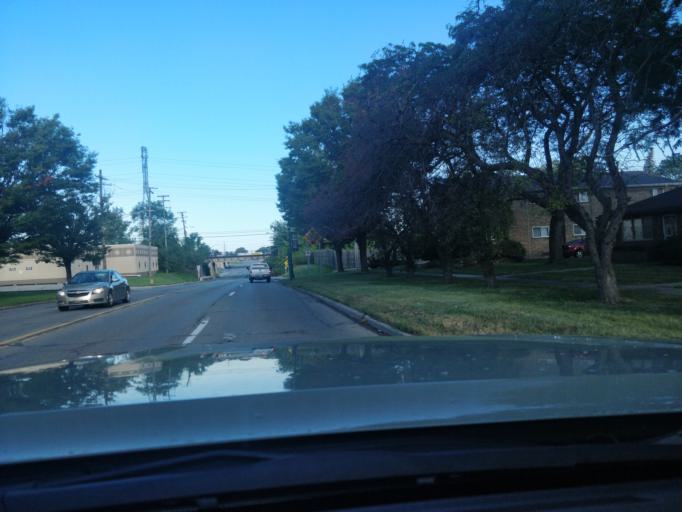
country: US
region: Michigan
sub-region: Wayne County
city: Melvindale
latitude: 42.2833
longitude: -83.1921
